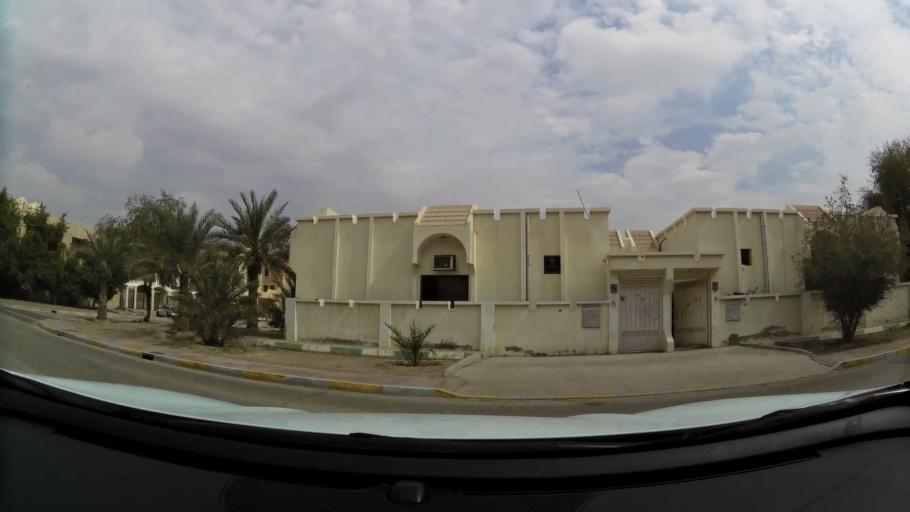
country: AE
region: Abu Dhabi
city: Al Ain
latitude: 24.2184
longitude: 55.7795
